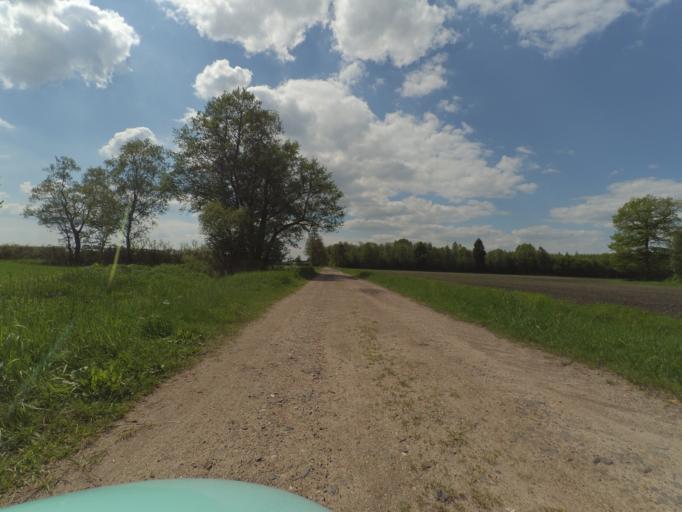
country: DE
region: Lower Saxony
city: Ummern
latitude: 52.5596
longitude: 10.4237
